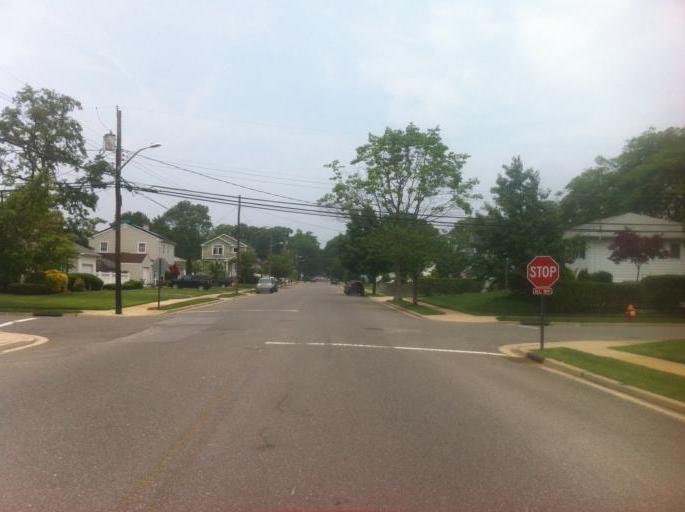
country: US
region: New York
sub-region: Nassau County
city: Seaford
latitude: 40.6688
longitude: -73.4781
